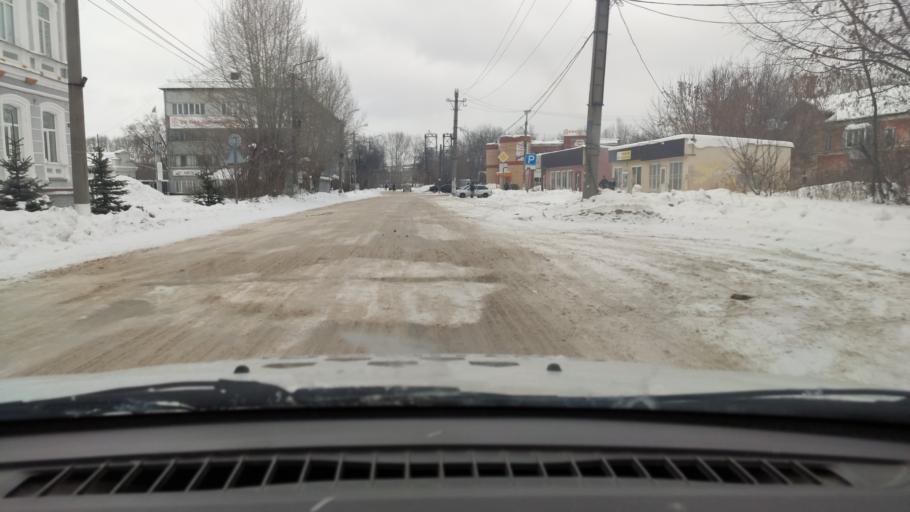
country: RU
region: Perm
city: Kungur
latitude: 57.4412
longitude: 56.9301
